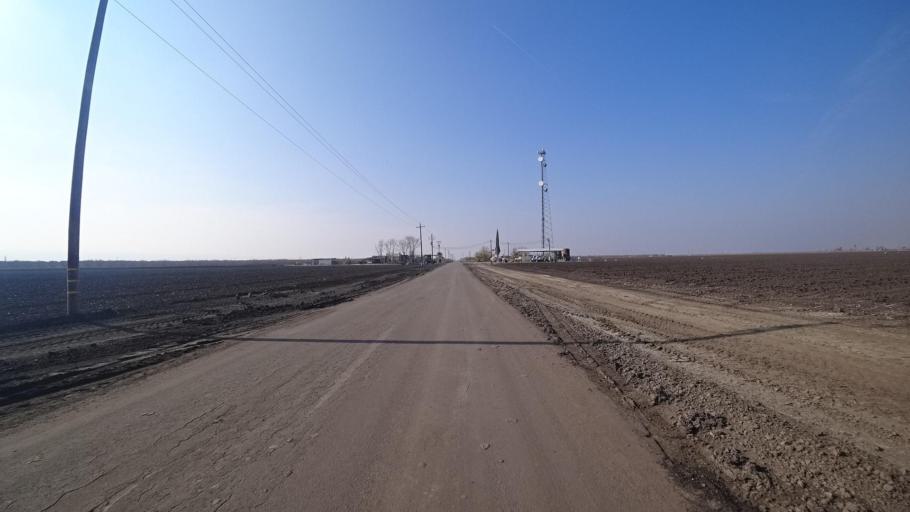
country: US
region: California
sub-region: Kern County
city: Buttonwillow
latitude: 35.3693
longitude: -119.4329
